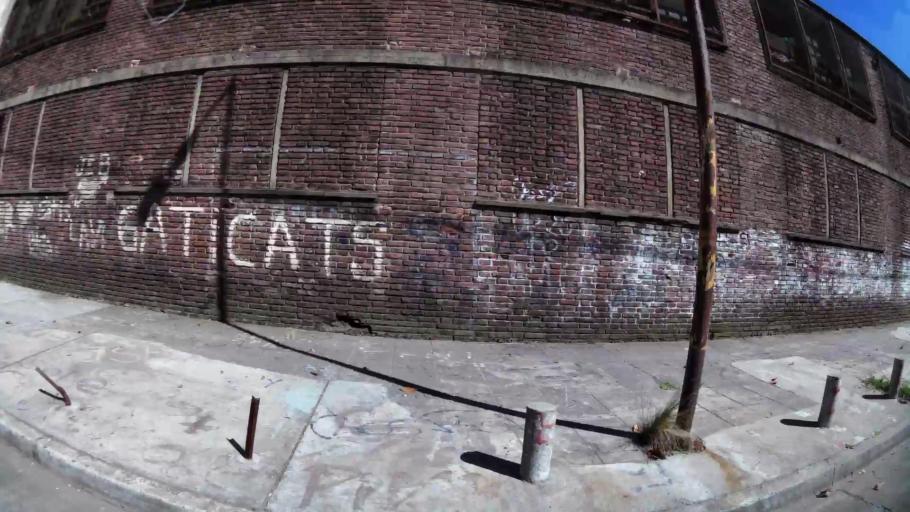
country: AR
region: Buenos Aires
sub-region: Partido de General San Martin
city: General San Martin
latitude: -34.5428
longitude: -58.5349
